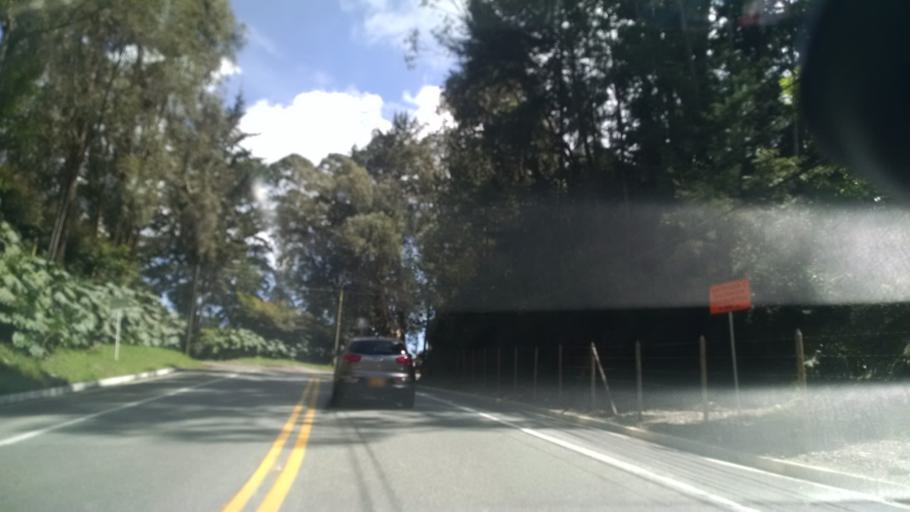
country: CO
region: Antioquia
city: El Retiro
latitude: 6.1127
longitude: -75.5015
